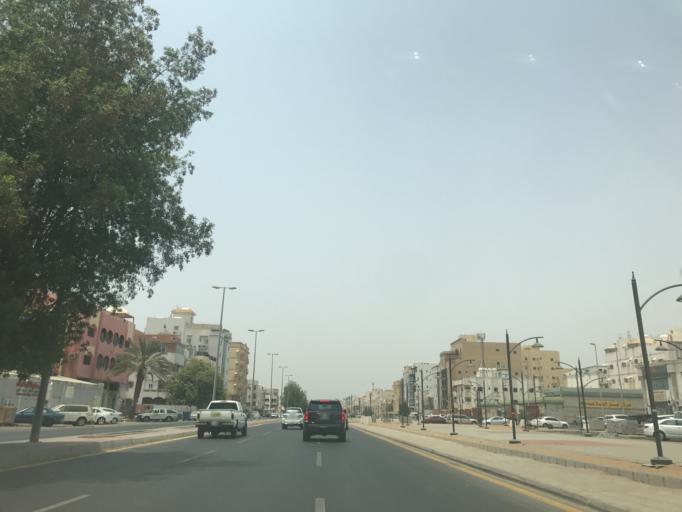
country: SA
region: Makkah
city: Jeddah
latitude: 21.5832
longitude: 39.1493
